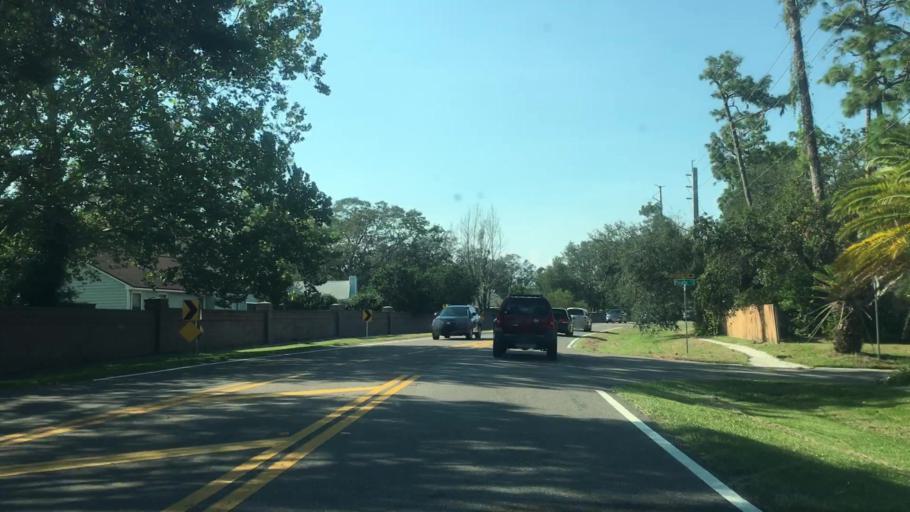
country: US
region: Florida
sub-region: Duval County
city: Neptune Beach
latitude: 30.3018
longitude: -81.4429
